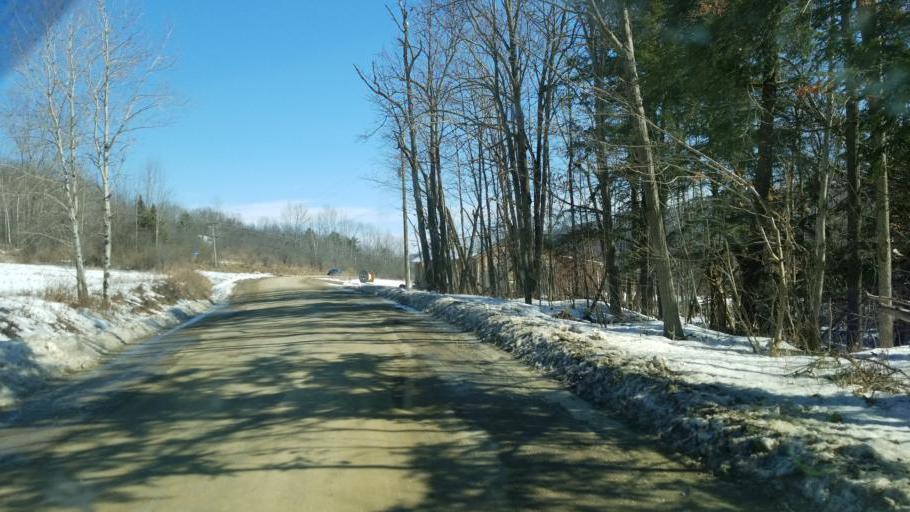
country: US
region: New York
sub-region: Allegany County
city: Alfred
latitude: 42.2482
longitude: -77.7037
